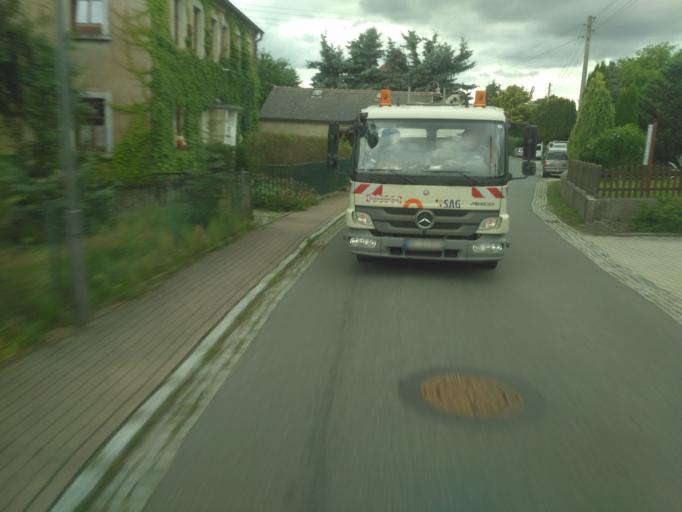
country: DE
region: Saxony
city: Lichtenberg
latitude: 51.1532
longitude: 13.9624
